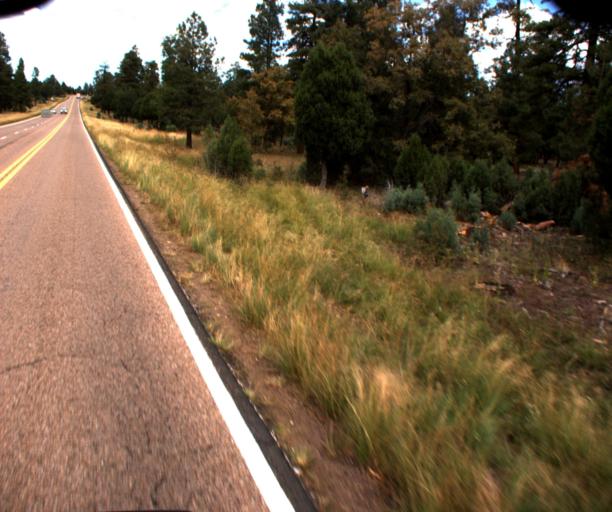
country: US
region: Arizona
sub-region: Navajo County
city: Heber-Overgaard
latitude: 34.3873
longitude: -110.6709
